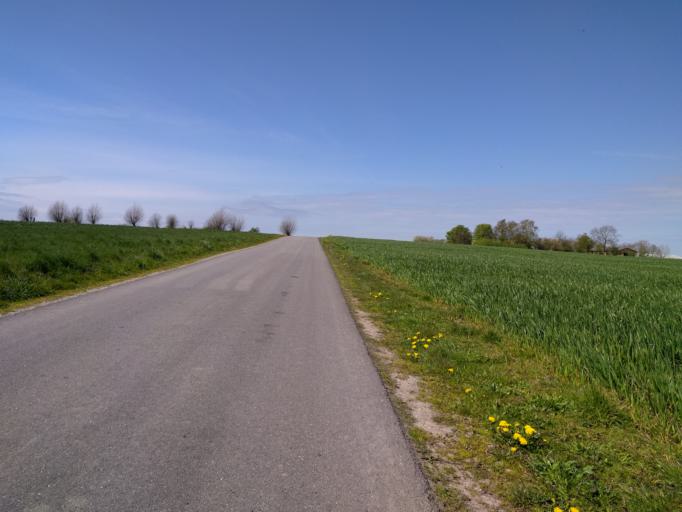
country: DK
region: South Denmark
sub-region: Kerteminde Kommune
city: Munkebo
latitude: 55.4446
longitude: 10.6012
